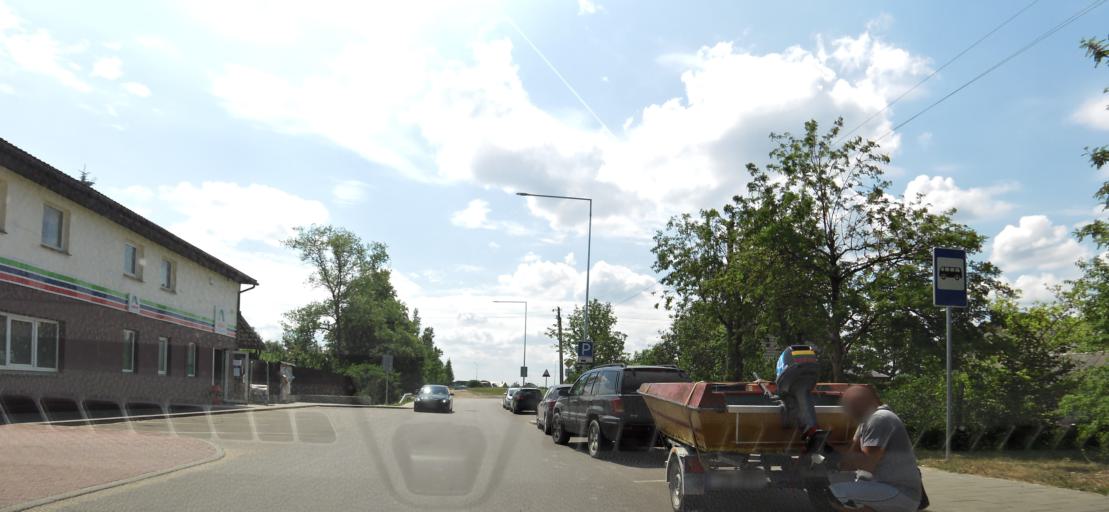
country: LT
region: Vilnius County
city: Pasilaiciai
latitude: 54.7597
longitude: 25.2075
